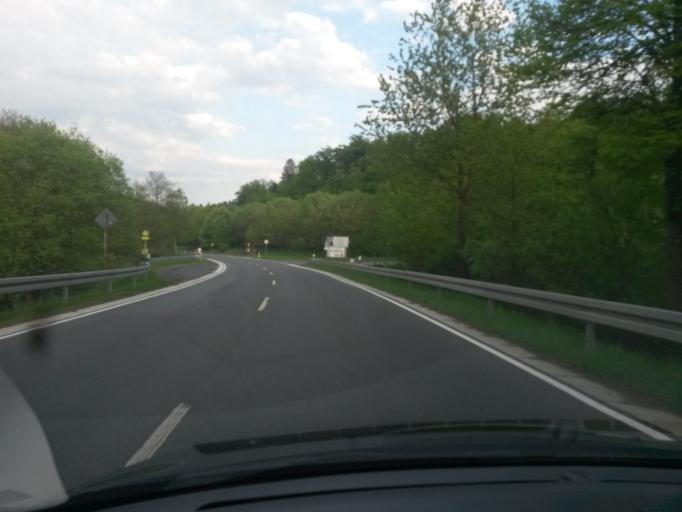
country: DE
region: Hesse
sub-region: Regierungsbezirk Kassel
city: Baunatal
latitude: 51.3095
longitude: 9.3791
